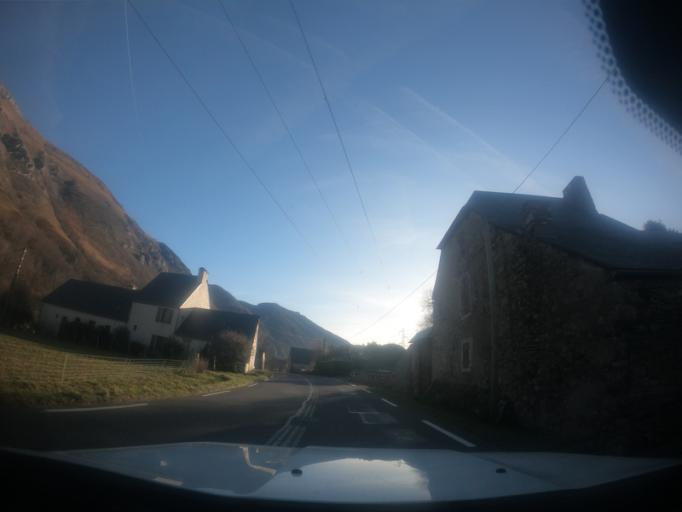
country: FR
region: Midi-Pyrenees
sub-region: Departement des Hautes-Pyrenees
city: Campan
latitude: 42.9961
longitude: 0.2072
